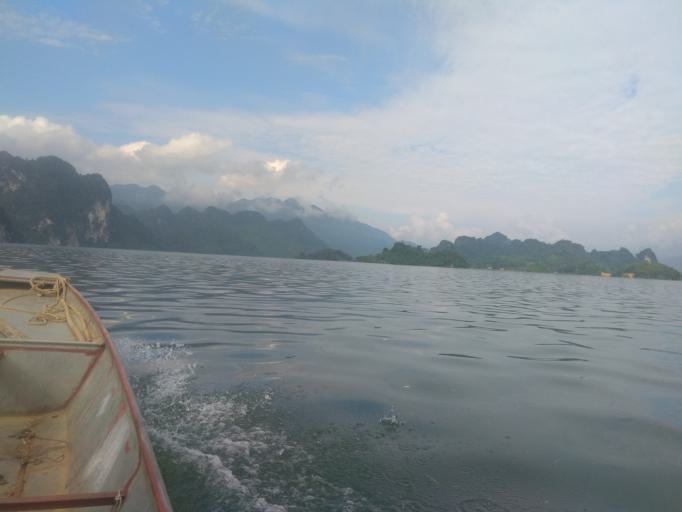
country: VN
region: Hoa Binh
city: Da Bac
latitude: 20.7563
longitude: 105.1502
